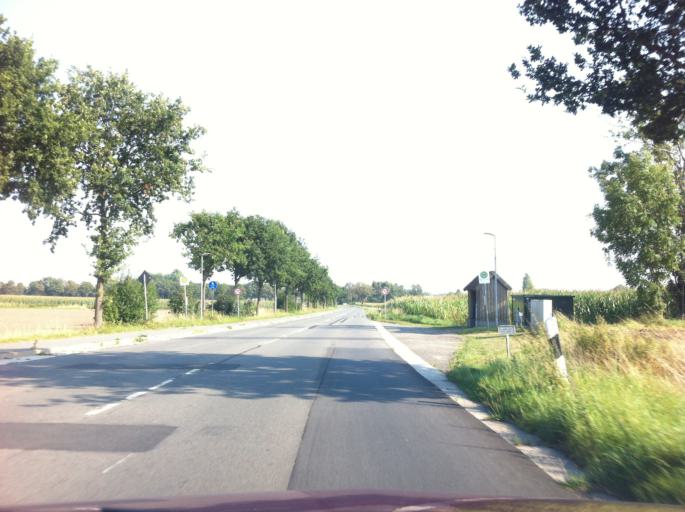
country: DE
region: Schleswig-Holstein
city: Oldenburg in Holstein
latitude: 54.3004
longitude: 10.8572
